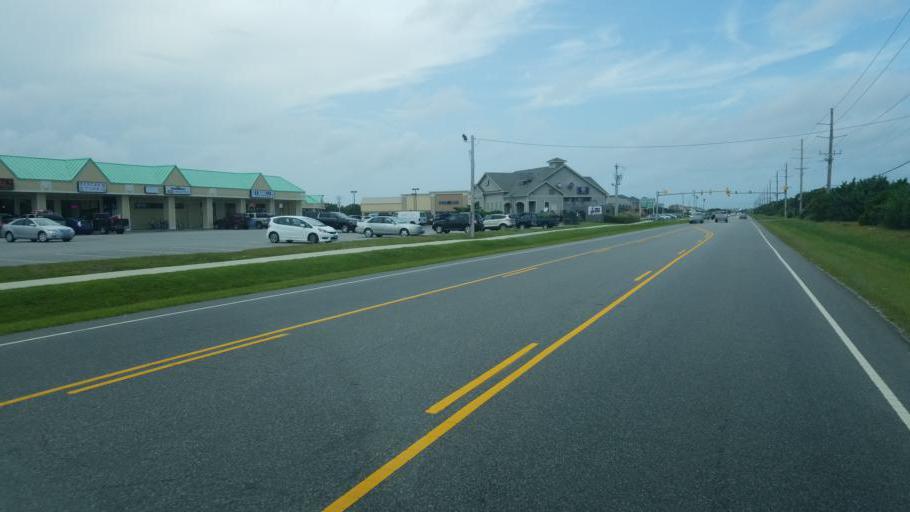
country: US
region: North Carolina
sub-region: Dare County
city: Buxton
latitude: 35.3321
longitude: -75.5072
